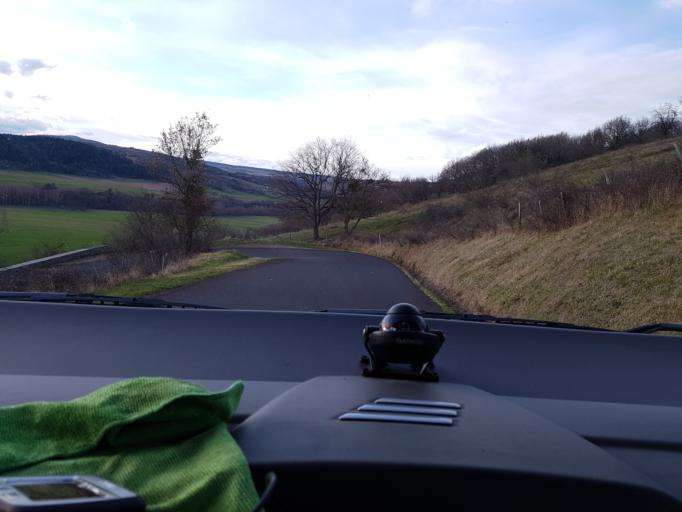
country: FR
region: Auvergne
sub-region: Departement du Cantal
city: Massiac
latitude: 45.2893
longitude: 3.1950
